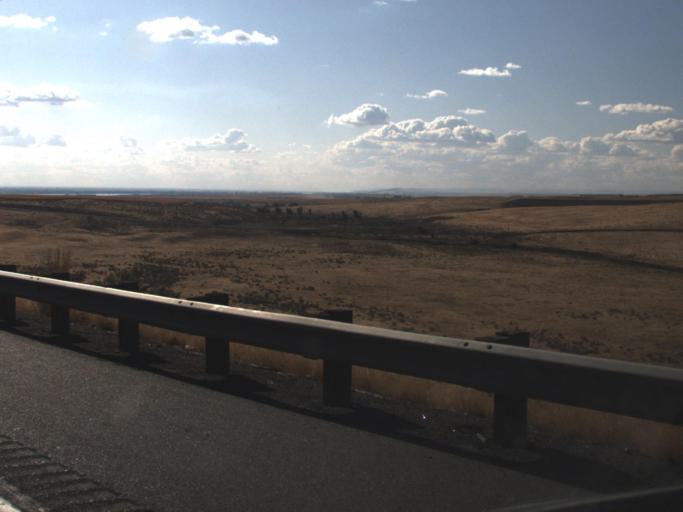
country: US
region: Oregon
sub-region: Umatilla County
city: Umatilla
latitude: 45.9727
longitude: -119.3375
